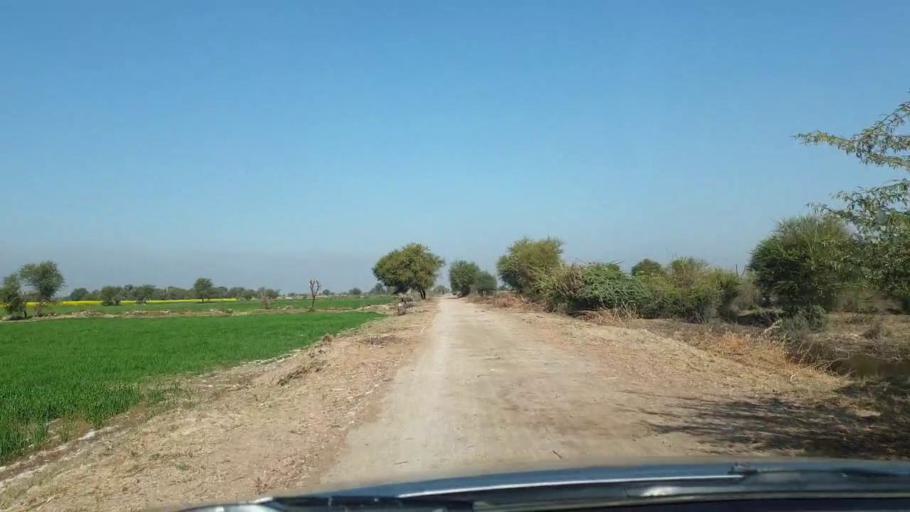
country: PK
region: Sindh
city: Jhol
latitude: 25.8828
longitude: 68.9053
